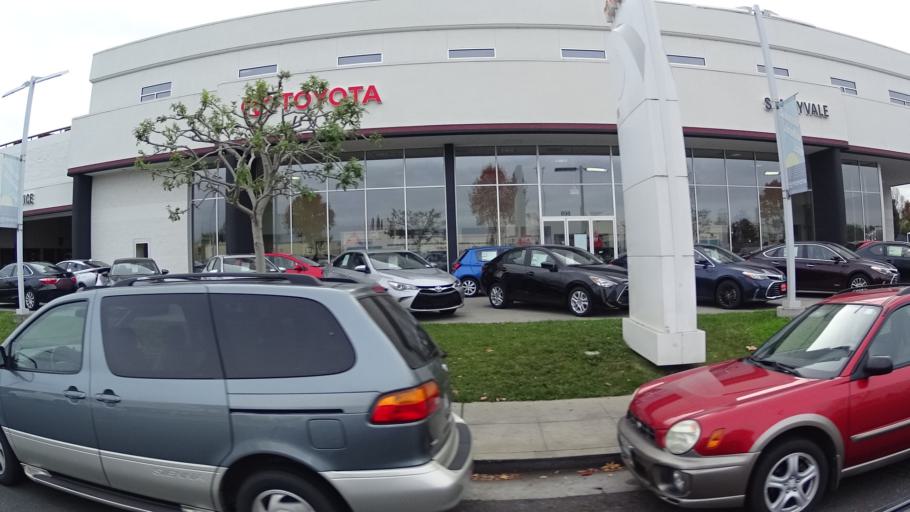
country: US
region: California
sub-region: Santa Clara County
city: Sunnyvale
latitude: 37.3709
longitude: -122.0444
